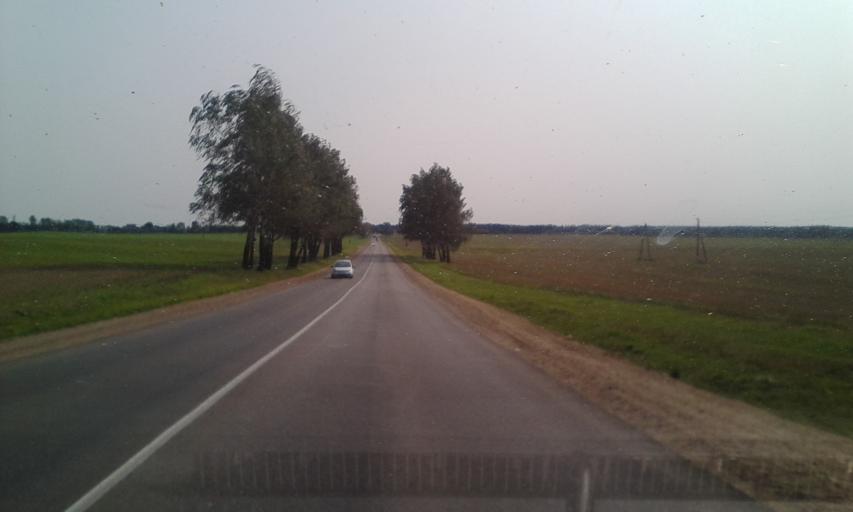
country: BY
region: Minsk
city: Hatava
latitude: 53.8241
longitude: 27.6287
